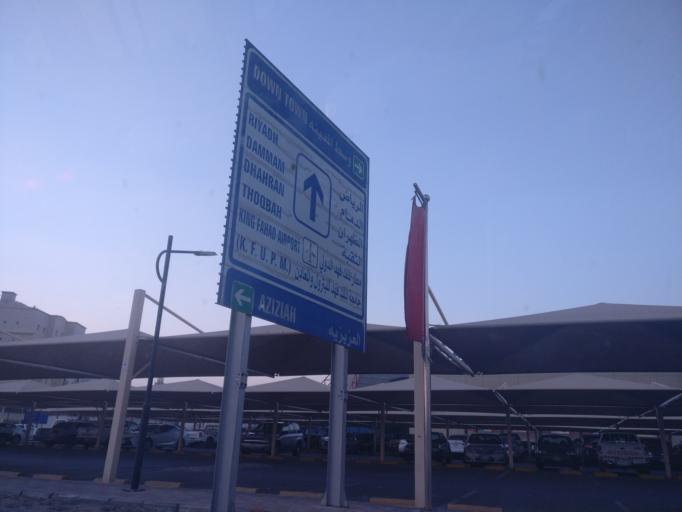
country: SA
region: Eastern Province
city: Khobar
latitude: 26.2665
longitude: 50.2140
